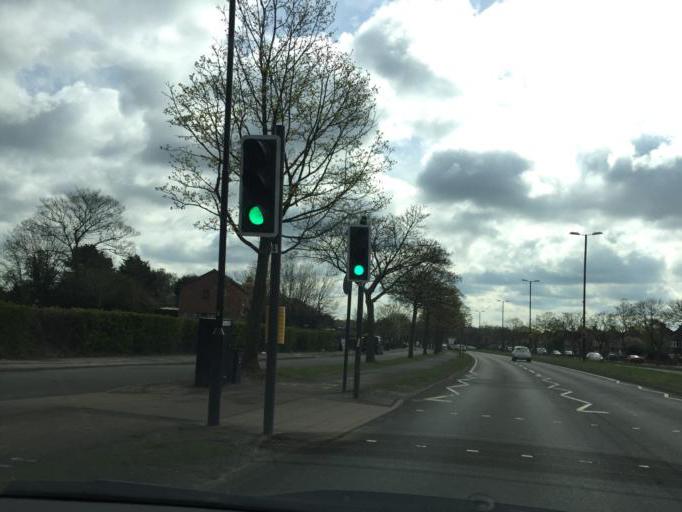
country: GB
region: England
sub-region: Coventry
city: Coventry
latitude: 52.3818
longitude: -1.5236
